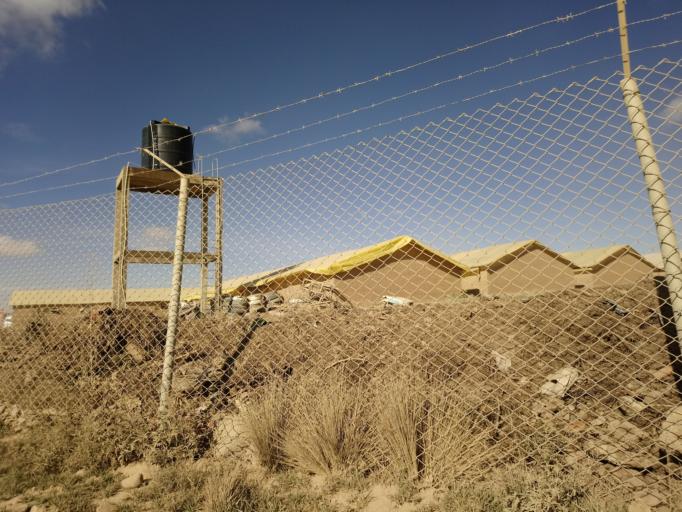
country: BO
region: La Paz
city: La Paz
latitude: -16.5108
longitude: -68.2125
